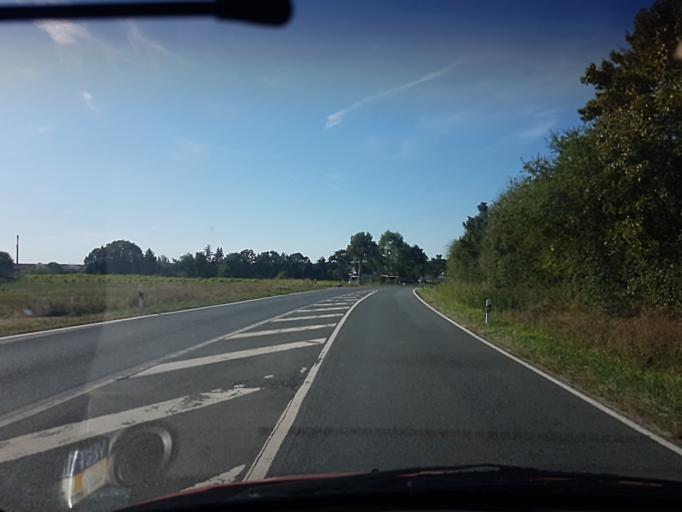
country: DE
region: Bavaria
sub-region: Regierungsbezirk Mittelfranken
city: Adelsdorf
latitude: 49.7077
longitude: 10.9072
